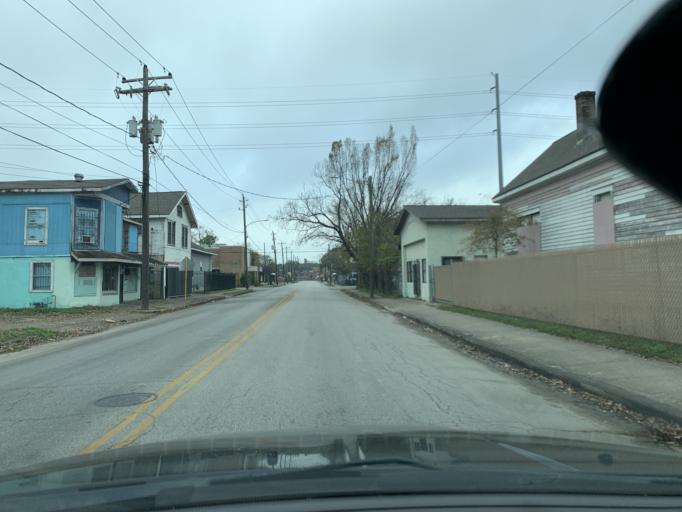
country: US
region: Texas
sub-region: Harris County
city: Houston
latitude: 29.7834
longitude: -95.3531
